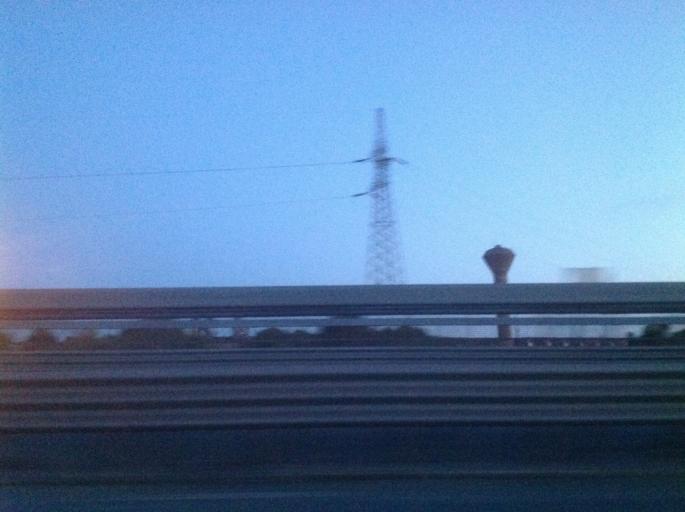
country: IT
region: Apulia
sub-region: Provincia di Taranto
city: Statte
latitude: 40.5132
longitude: 17.1803
